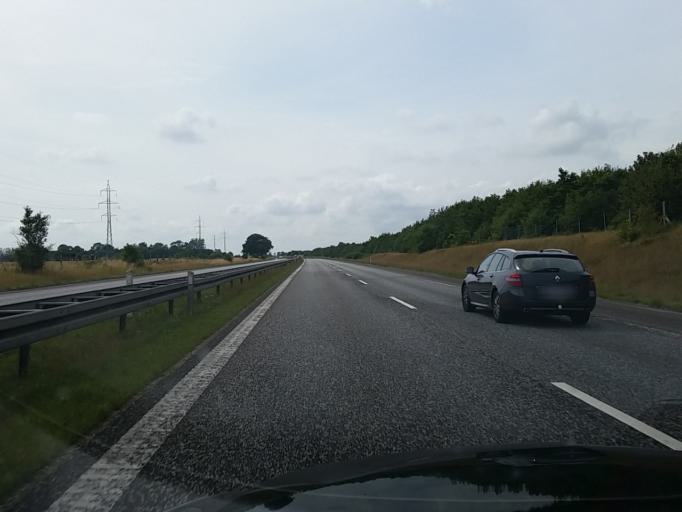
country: DK
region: South Denmark
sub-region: Kolding Kommune
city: Lunderskov
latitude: 55.5074
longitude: 9.3208
